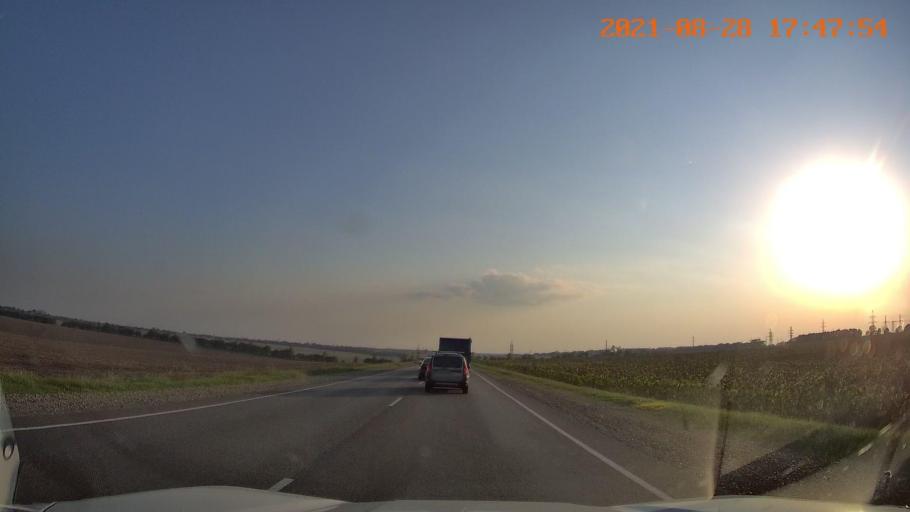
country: RU
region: Krasnodarskiy
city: Novoalekseyevskaya
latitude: 44.9683
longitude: 40.8463
